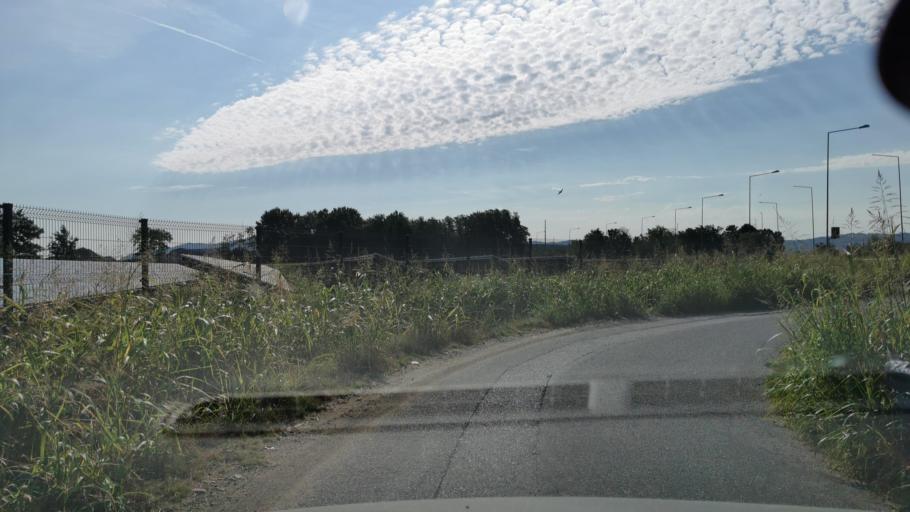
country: IT
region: Piedmont
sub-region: Provincia di Torino
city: Settimo Torinese
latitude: 45.1601
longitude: 7.7760
